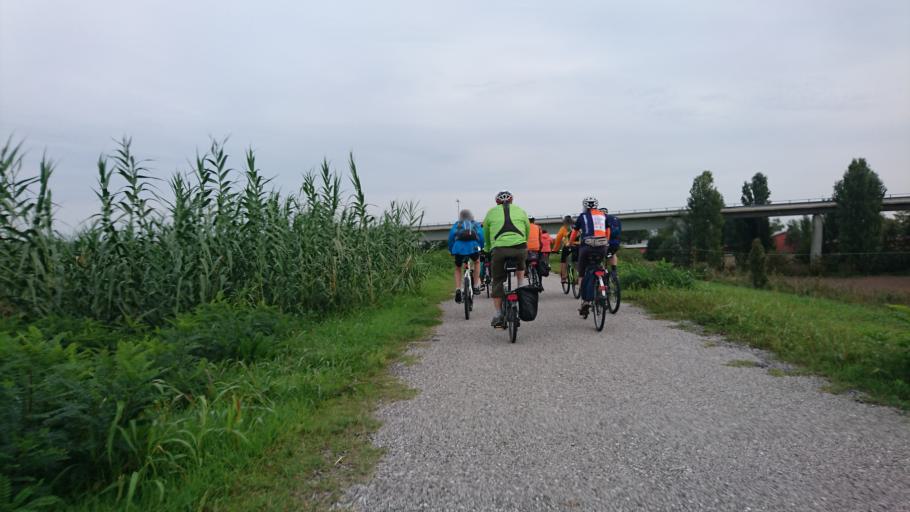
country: IT
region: Veneto
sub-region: Provincia di Rovigo
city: Ca' Tiepolo
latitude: 44.9551
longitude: 12.3596
